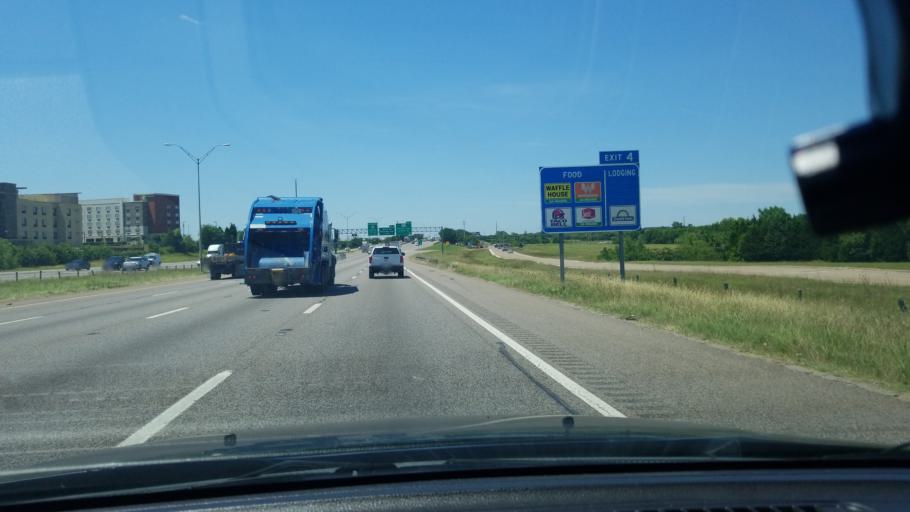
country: US
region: Texas
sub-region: Dallas County
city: Mesquite
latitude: 32.7631
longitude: -96.6200
